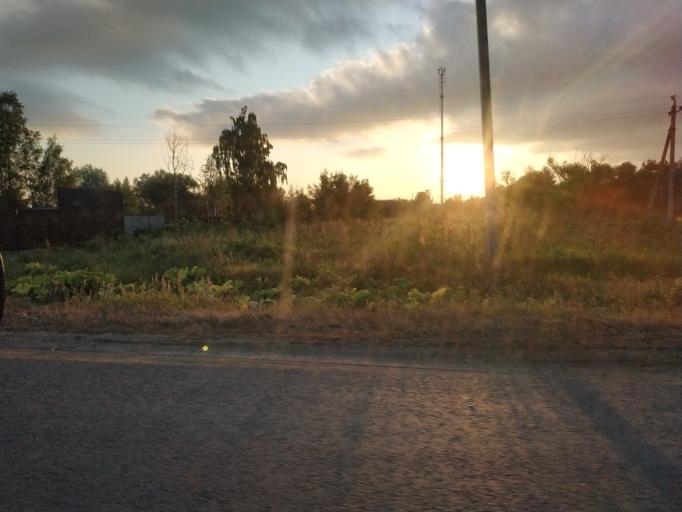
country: RU
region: Moskovskaya
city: Krasnoarmeysk
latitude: 56.0231
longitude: 38.1765
